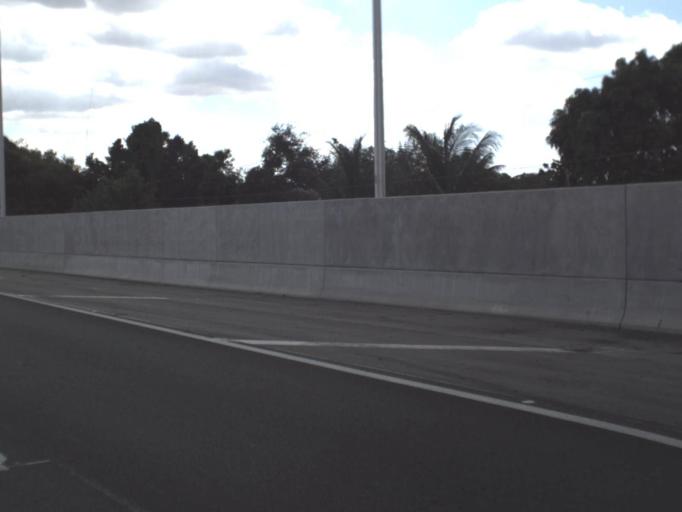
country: US
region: Florida
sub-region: Broward County
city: Pembroke Pines
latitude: 26.0157
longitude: -80.2129
